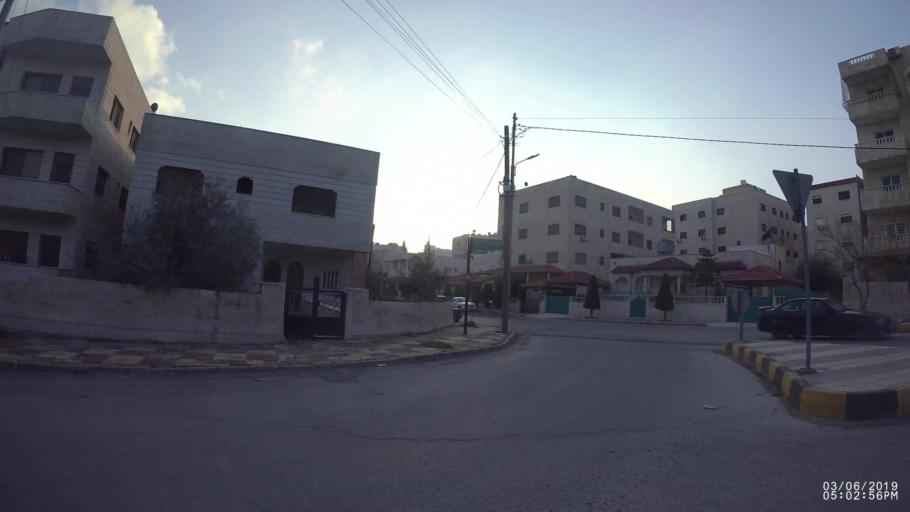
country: JO
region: Amman
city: Amman
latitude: 31.9943
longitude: 35.9532
